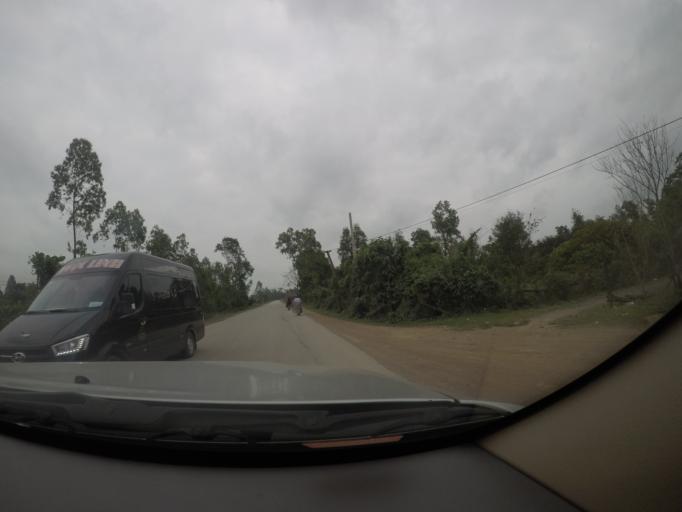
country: VN
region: Quang Binh
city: Quan Hau
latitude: 17.3131
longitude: 106.6329
